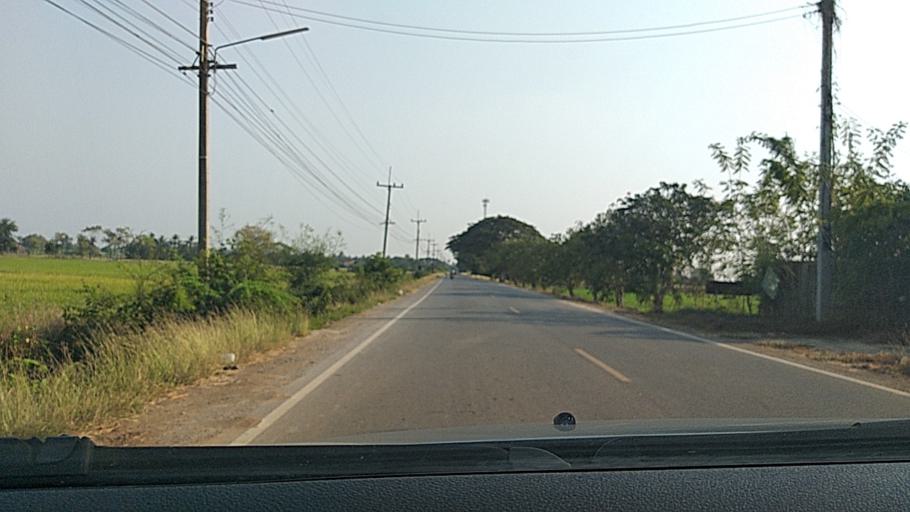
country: TH
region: Sing Buri
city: Sing Buri
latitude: 14.8492
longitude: 100.3908
